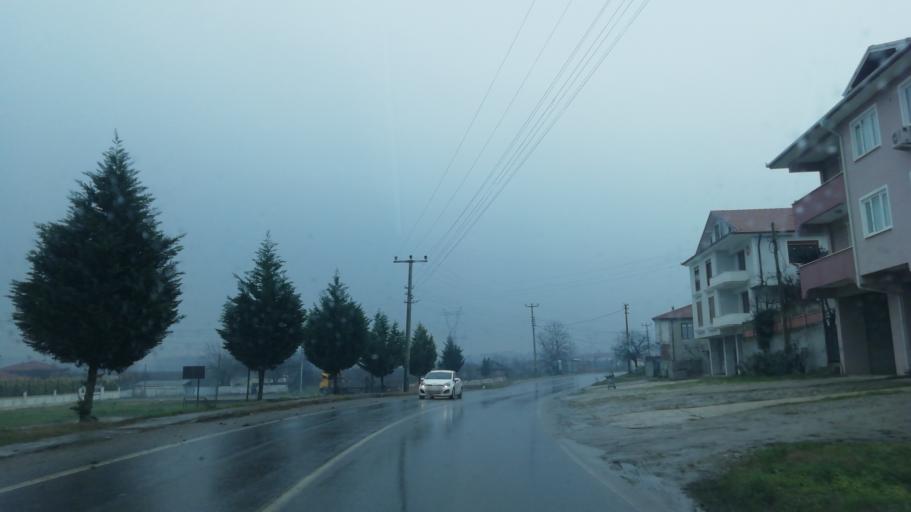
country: TR
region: Sakarya
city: Karapurcek
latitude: 40.6898
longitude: 30.5003
